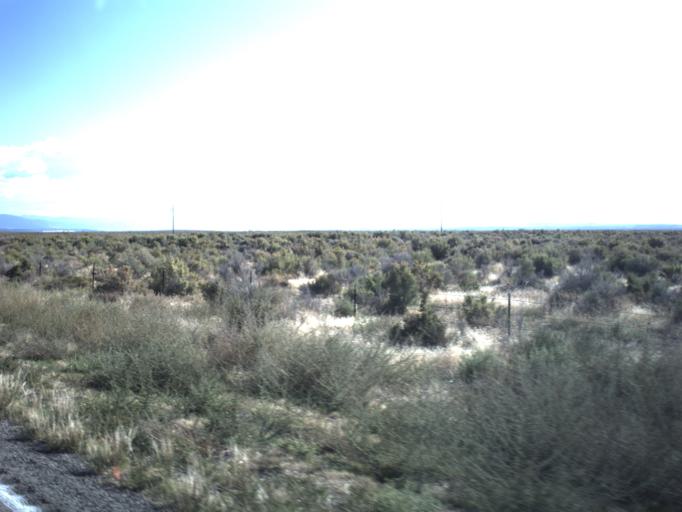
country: US
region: Utah
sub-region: Millard County
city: Delta
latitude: 39.2320
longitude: -112.4278
